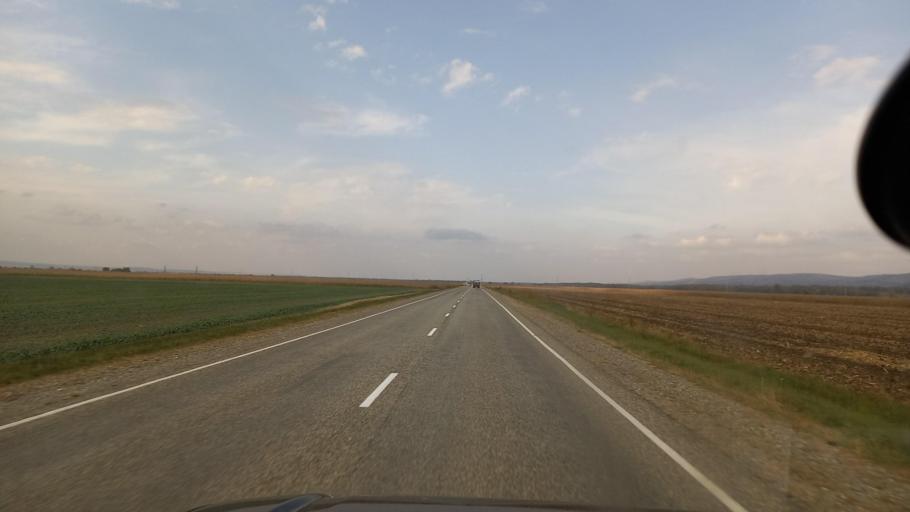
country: RU
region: Krasnodarskiy
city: Perepravnaya
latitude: 44.3127
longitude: 40.8562
